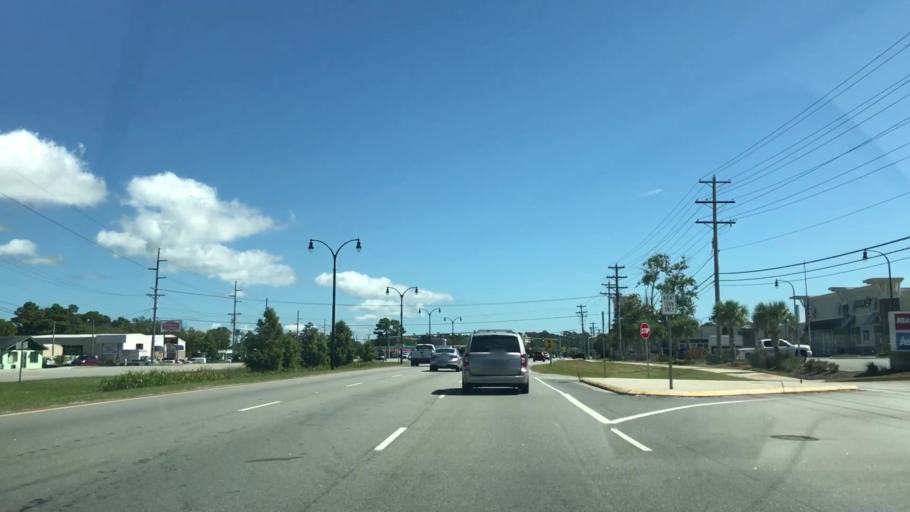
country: US
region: South Carolina
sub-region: Horry County
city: North Myrtle Beach
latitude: 33.8408
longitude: -78.6640
